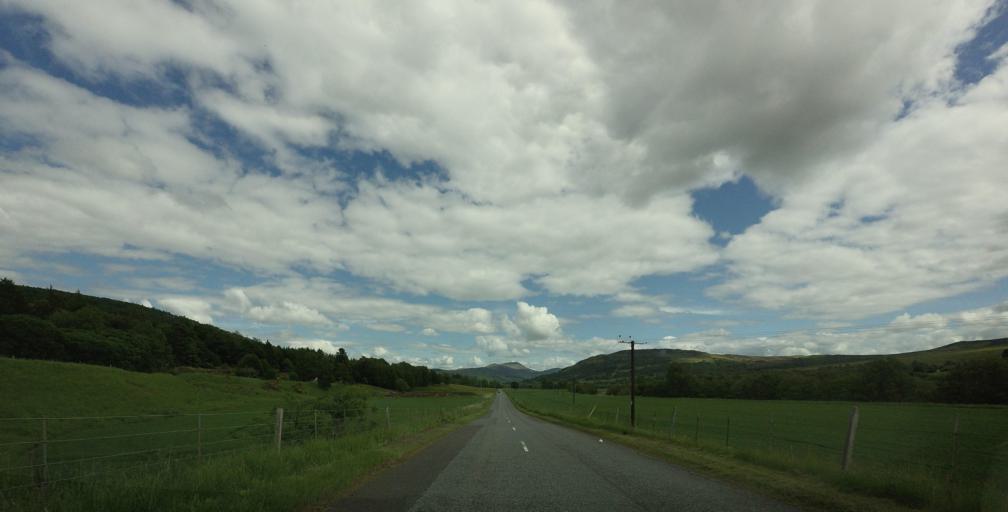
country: GB
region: Scotland
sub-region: Perth and Kinross
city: Aberfeldy
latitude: 56.7711
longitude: -3.9237
